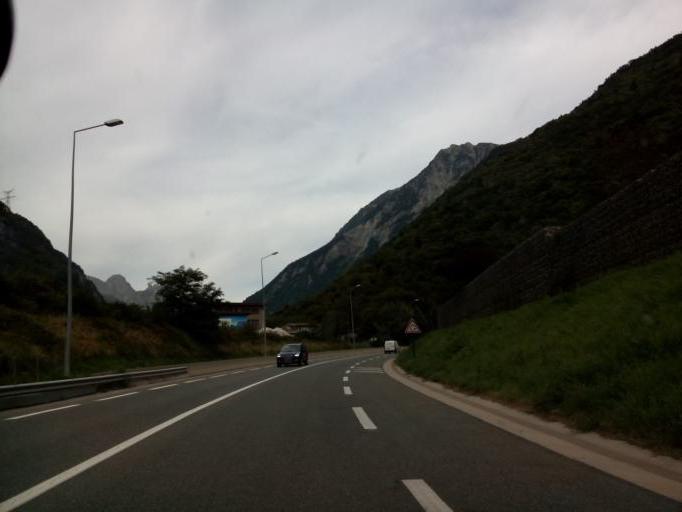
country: FR
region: Rhone-Alpes
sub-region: Departement de l'Isere
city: Vaulnaveys-le-Bas
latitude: 45.0718
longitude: 5.8726
